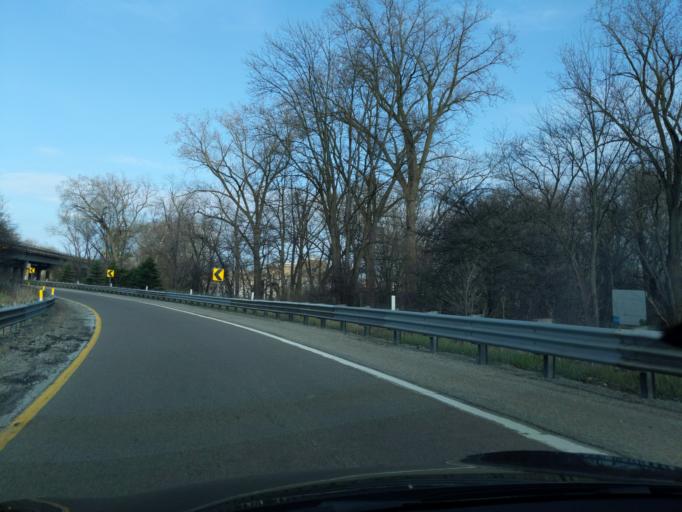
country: US
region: Michigan
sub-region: Ingham County
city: East Lansing
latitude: 42.7236
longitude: -84.5152
